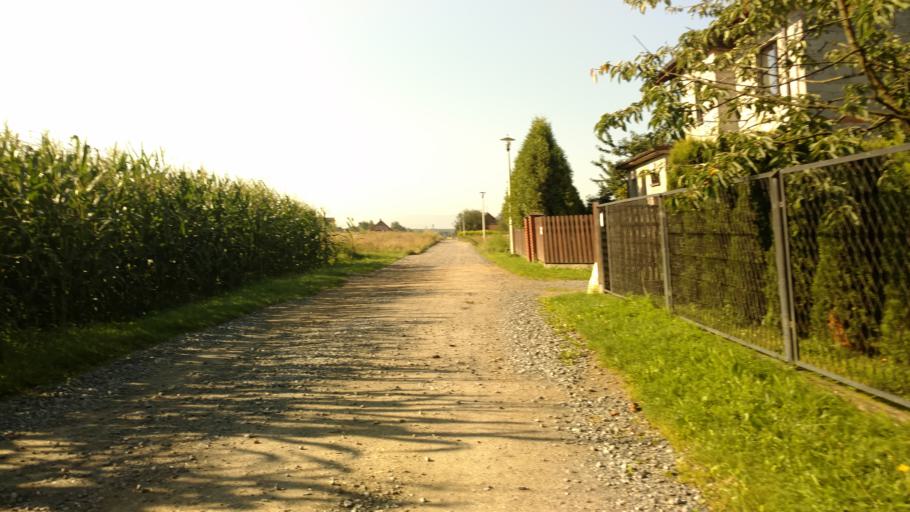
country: PL
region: Silesian Voivodeship
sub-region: Powiat pszczynski
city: Pszczyna
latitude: 49.9922
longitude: 18.9672
